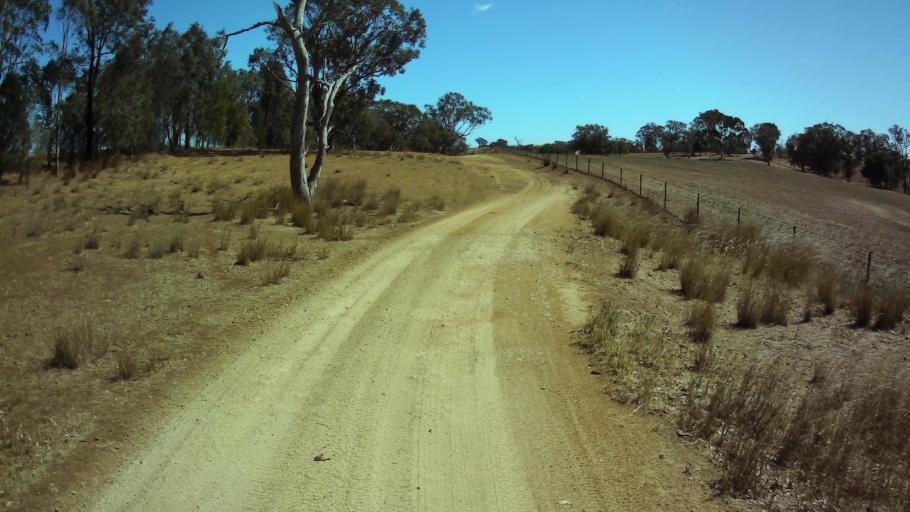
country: AU
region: New South Wales
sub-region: Weddin
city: Grenfell
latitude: -33.9940
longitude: 148.4366
